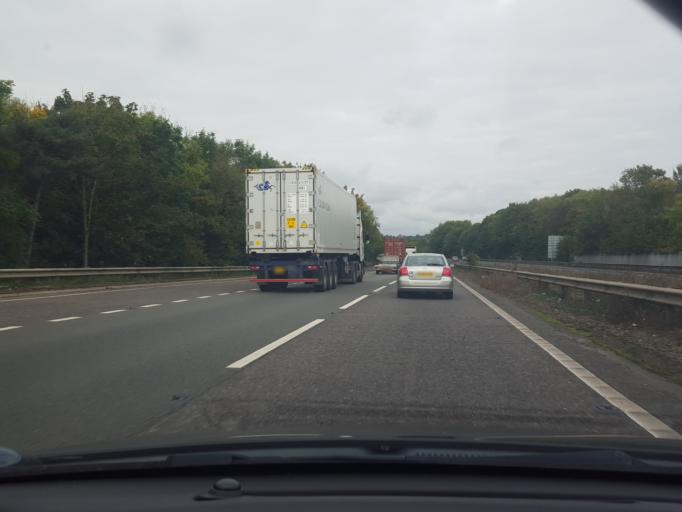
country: GB
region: England
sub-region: Suffolk
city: Bramford
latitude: 52.1080
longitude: 1.1060
